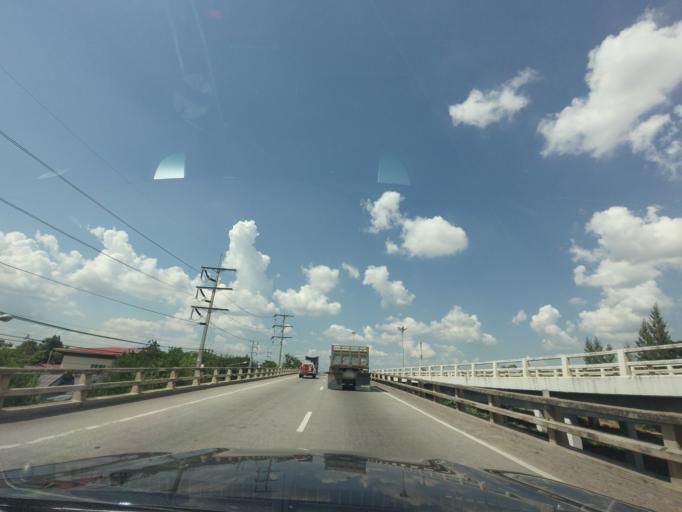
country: TH
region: Nakhon Ratchasima
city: Nakhon Ratchasima
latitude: 14.9637
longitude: 102.0529
